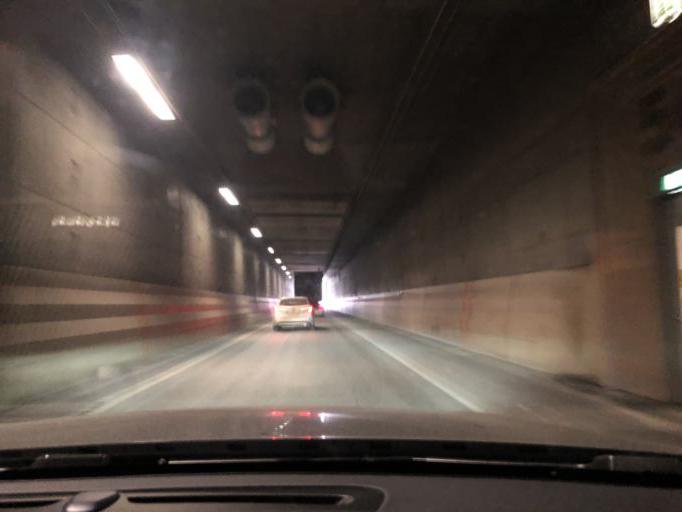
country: SE
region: Stockholm
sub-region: Stockholms Kommun
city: Arsta
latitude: 59.2909
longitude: 18.0808
